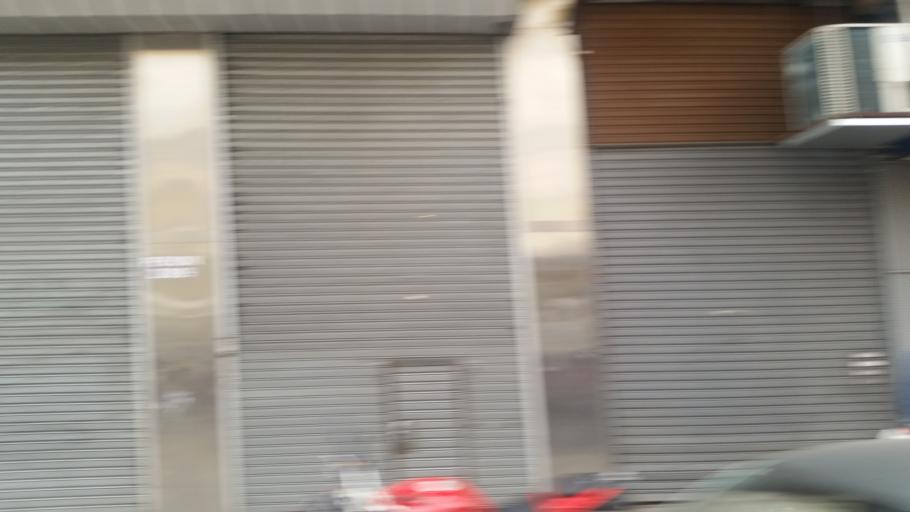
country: AR
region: Buenos Aires F.D.
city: Buenos Aires
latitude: -34.6077
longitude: -58.4064
